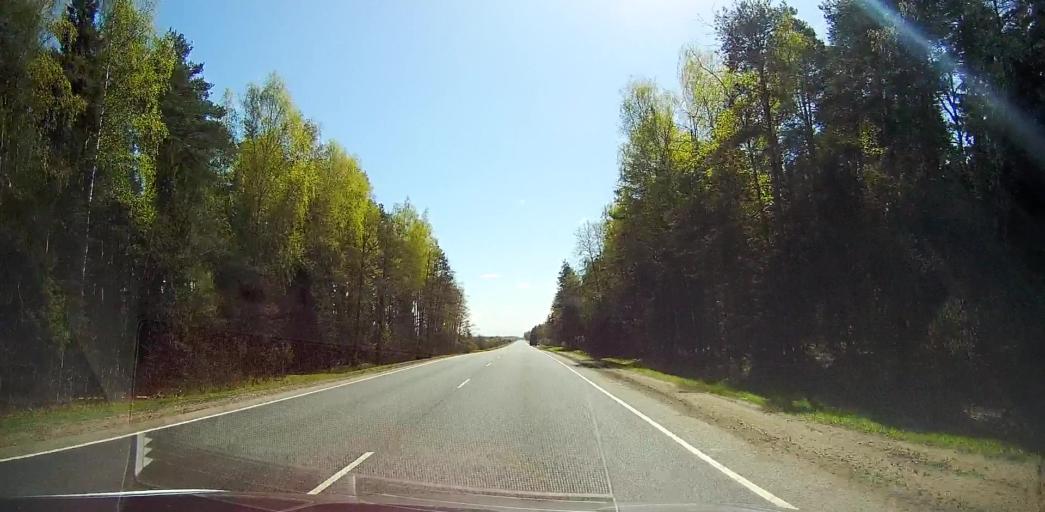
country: RU
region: Moskovskaya
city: Gzhel'
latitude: 55.6011
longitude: 38.3783
